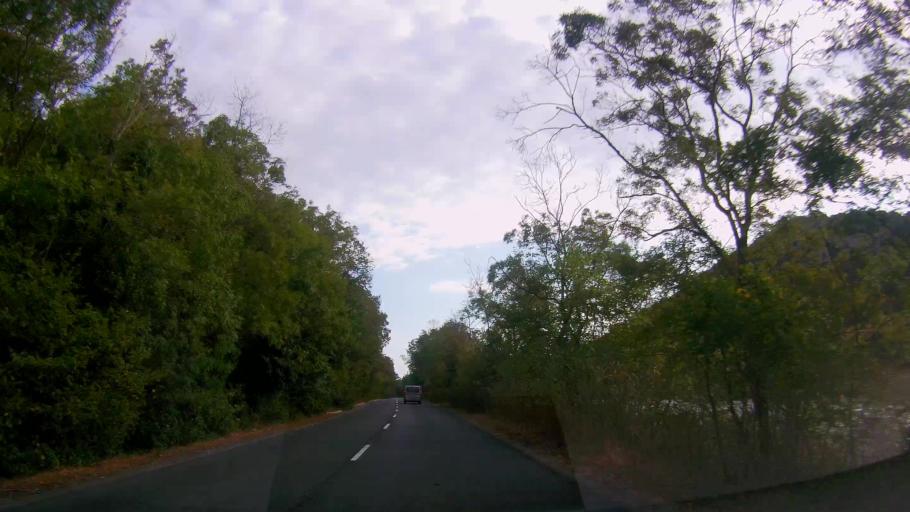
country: BG
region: Burgas
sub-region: Obshtina Primorsko
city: Primorsko
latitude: 42.3158
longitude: 27.7293
